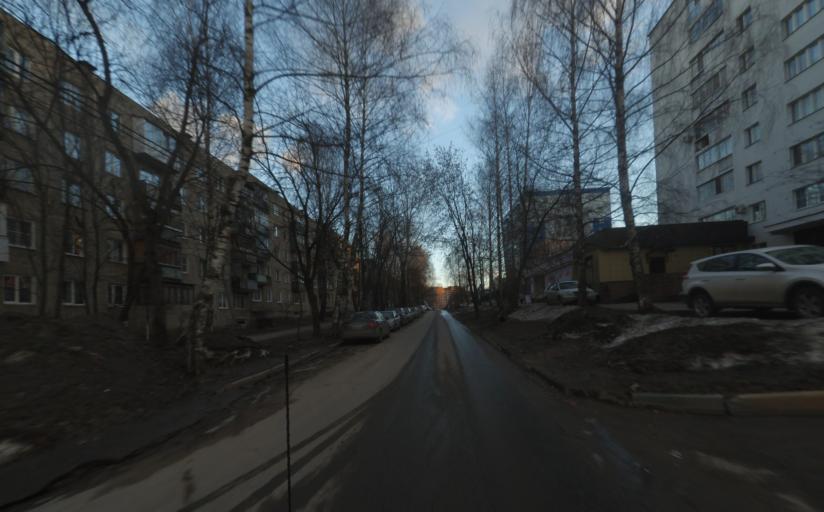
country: RU
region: Nizjnij Novgorod
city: Afonino
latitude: 56.2868
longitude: 44.0454
